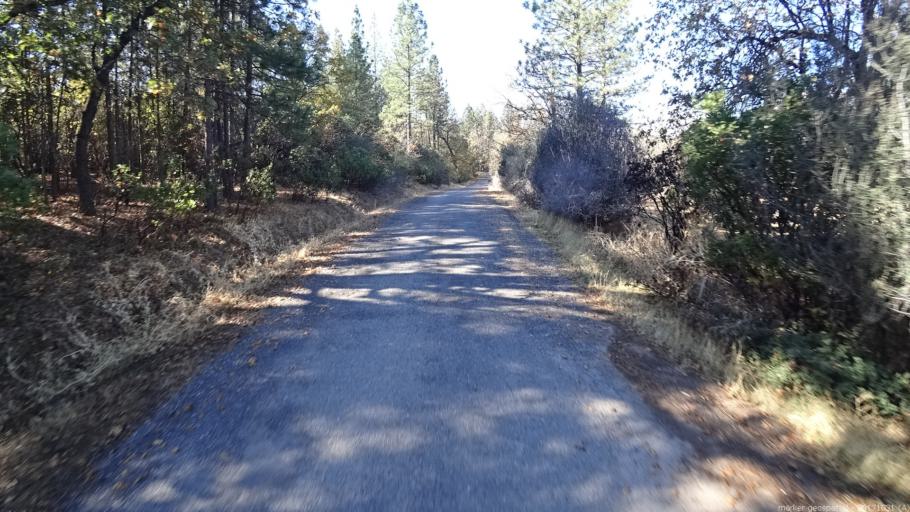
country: US
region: California
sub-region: Shasta County
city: Shingletown
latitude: 40.4466
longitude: -121.8337
